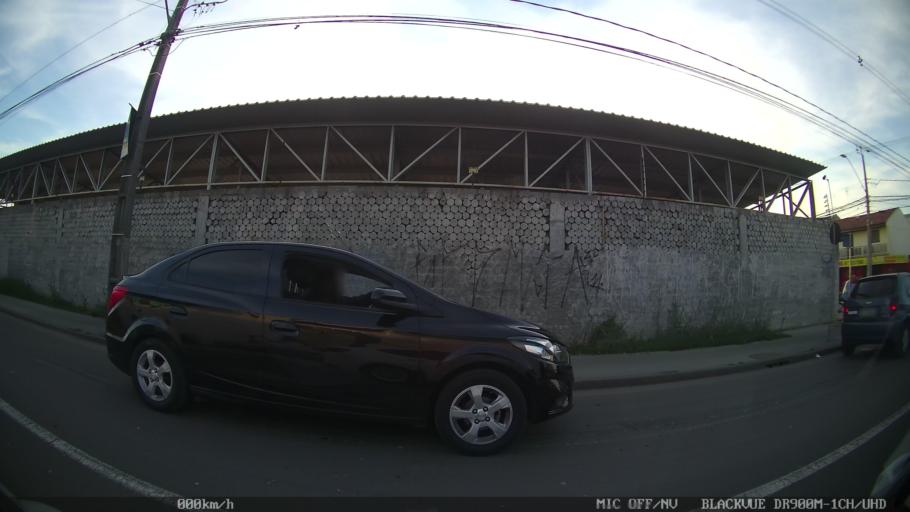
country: BR
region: Parana
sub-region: Pinhais
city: Pinhais
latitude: -25.4407
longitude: -49.1756
